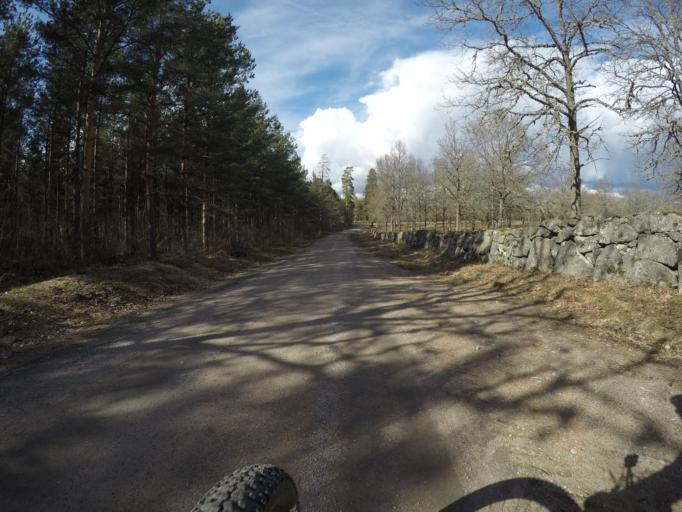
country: SE
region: Vaestmanland
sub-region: Kungsors Kommun
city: Kungsoer
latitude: 59.2777
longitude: 16.1225
